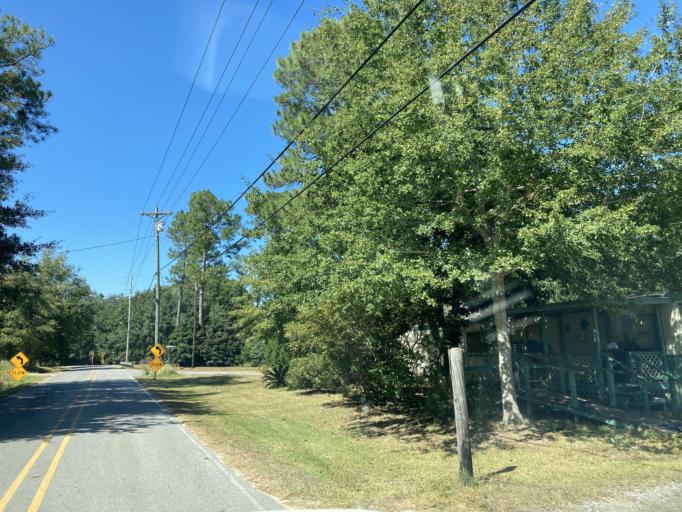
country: US
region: Mississippi
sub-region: Jackson County
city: Saint Martin
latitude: 30.4605
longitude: -88.8701
